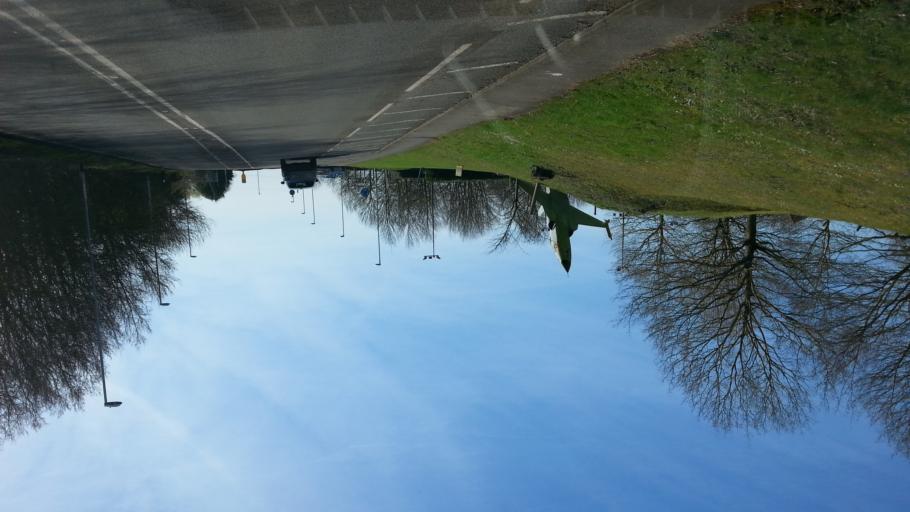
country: GB
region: England
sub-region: Cambridgeshire
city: Great Stukeley
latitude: 52.3637
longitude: -0.2247
